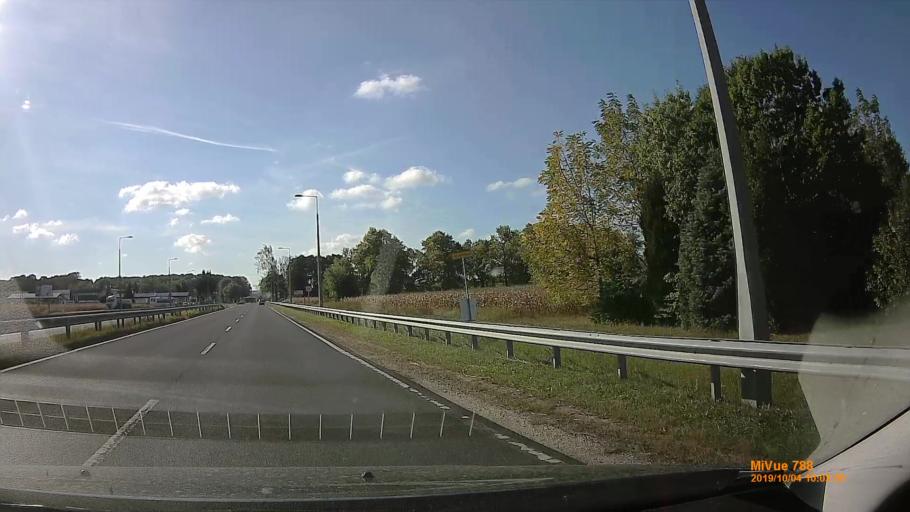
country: HU
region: Somogy
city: Kaposvar
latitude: 46.3925
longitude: 17.7777
